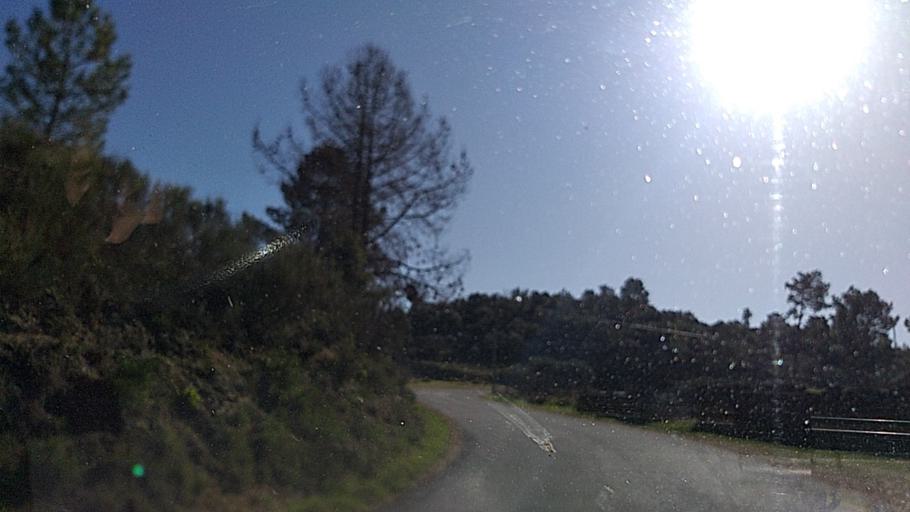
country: PT
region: Guarda
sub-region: Celorico da Beira
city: Celorico da Beira
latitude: 40.6836
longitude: -7.3977
